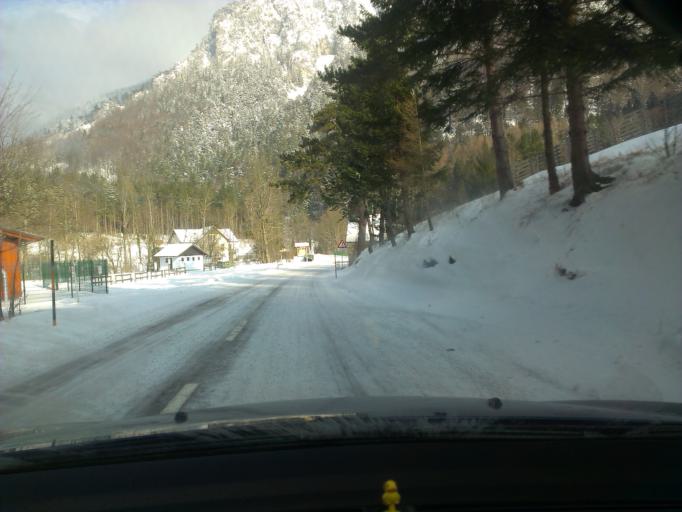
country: AT
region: Lower Austria
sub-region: Politischer Bezirk Neunkirchen
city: Reichenau an der Rax
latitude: 47.7337
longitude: 15.7923
